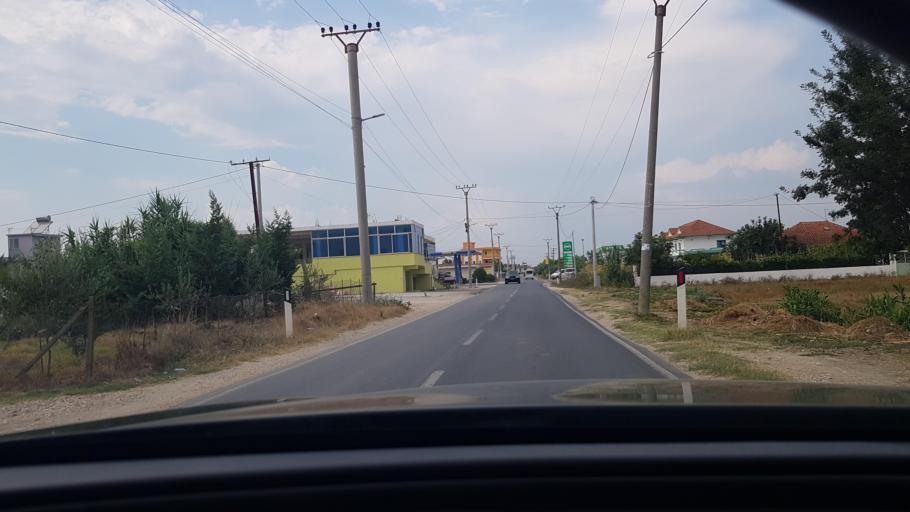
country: AL
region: Durres
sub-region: Rrethi i Durresit
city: Katundi i Ri
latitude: 41.4236
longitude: 19.5483
